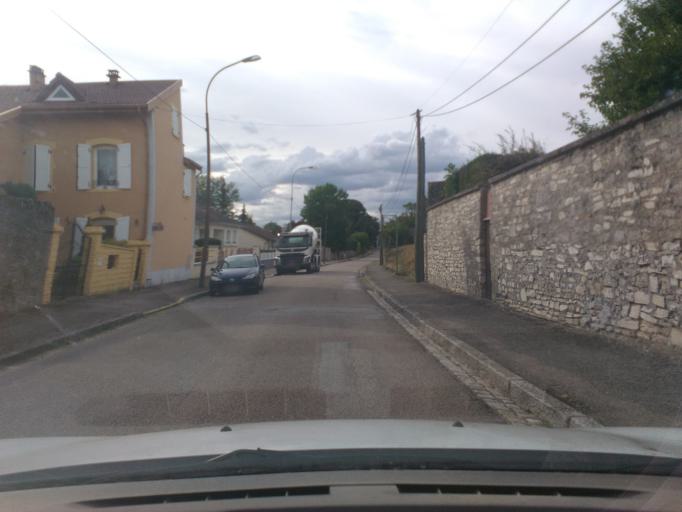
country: FR
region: Lorraine
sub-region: Departement des Vosges
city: Chatel-sur-Moselle
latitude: 48.3148
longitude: 6.3909
